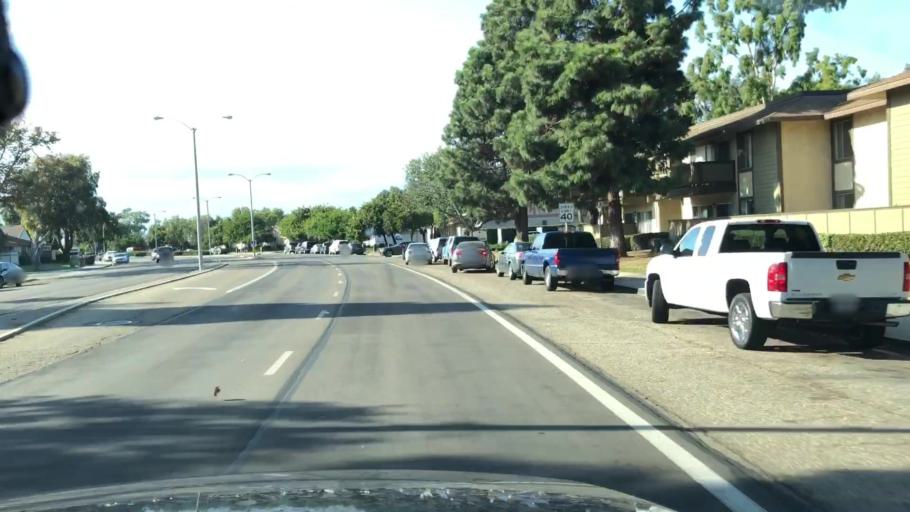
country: US
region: California
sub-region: Ventura County
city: El Rio
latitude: 34.2282
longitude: -119.1828
